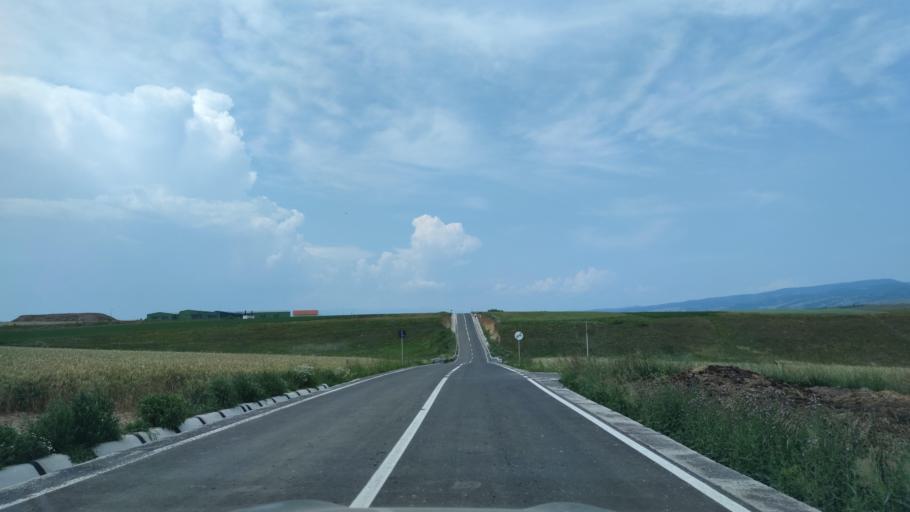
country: RO
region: Harghita
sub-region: Comuna Subcetate
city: Subcetate
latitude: 46.8231
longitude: 25.4473
